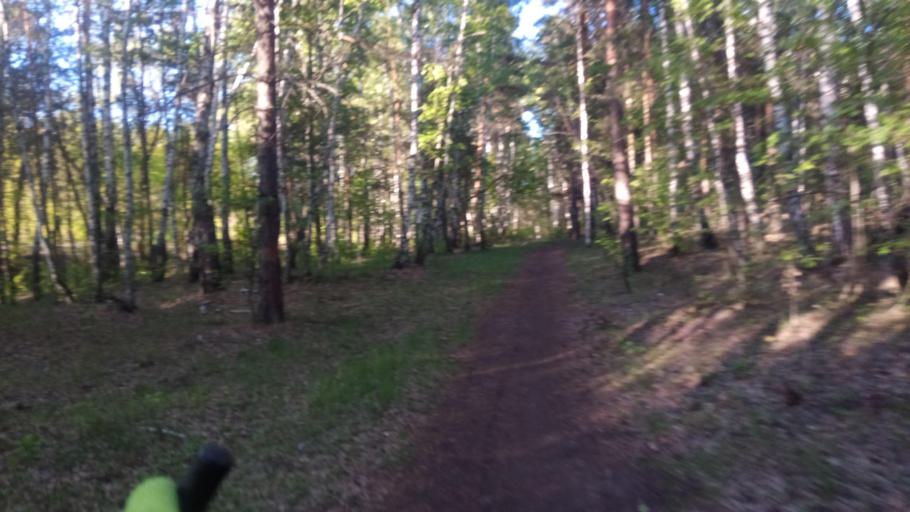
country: RU
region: Chelyabinsk
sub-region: Gorod Chelyabinsk
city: Chelyabinsk
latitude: 55.1510
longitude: 61.3327
